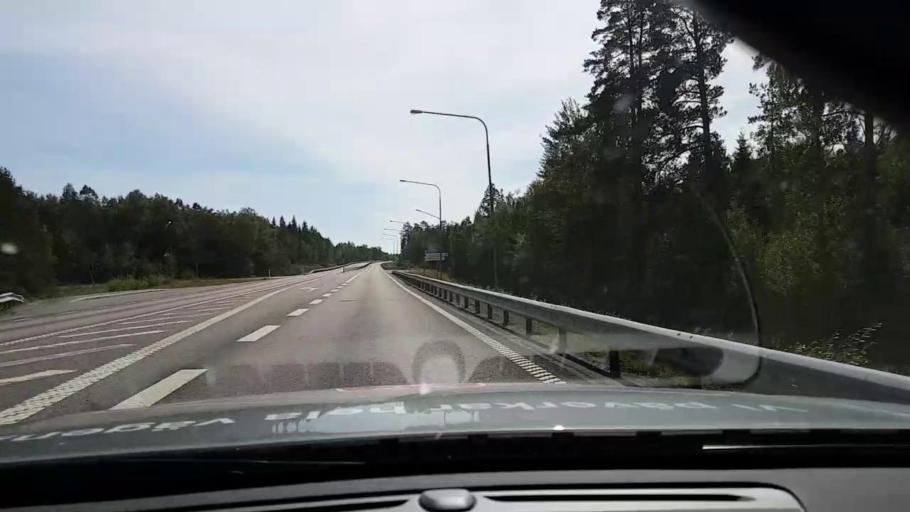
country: SE
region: Vaesternorrland
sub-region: OErnskoeldsviks Kommun
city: Husum
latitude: 63.3762
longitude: 19.1903
